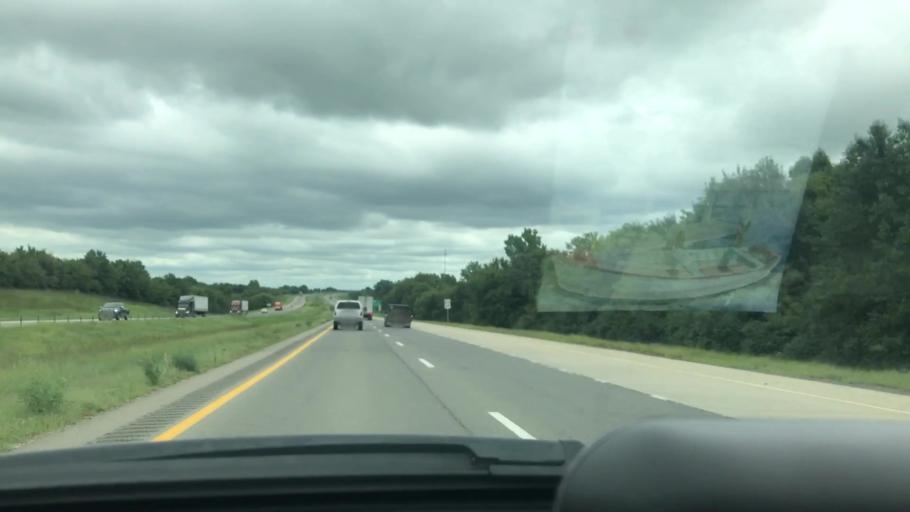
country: US
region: Oklahoma
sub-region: McIntosh County
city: Checotah
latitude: 35.4796
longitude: -95.5340
